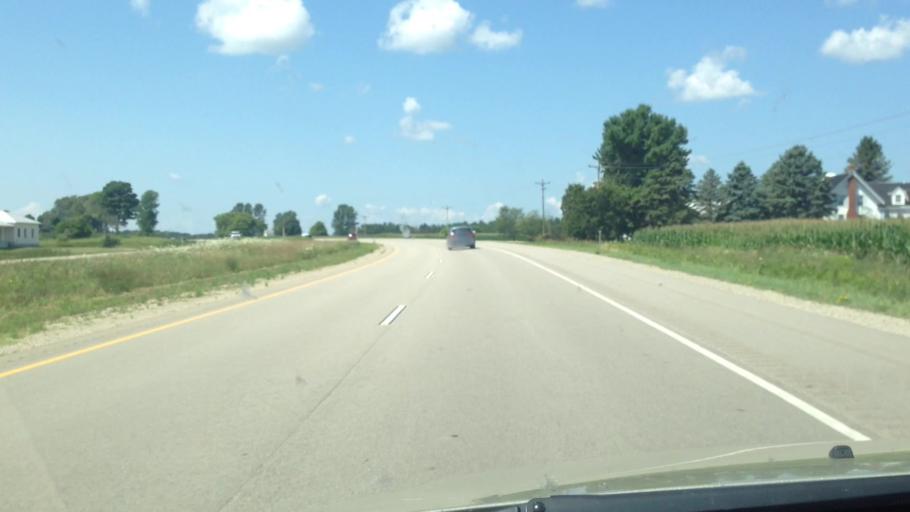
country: US
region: Wisconsin
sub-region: Oconto County
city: Oconto Falls
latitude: 44.8004
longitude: -88.0173
